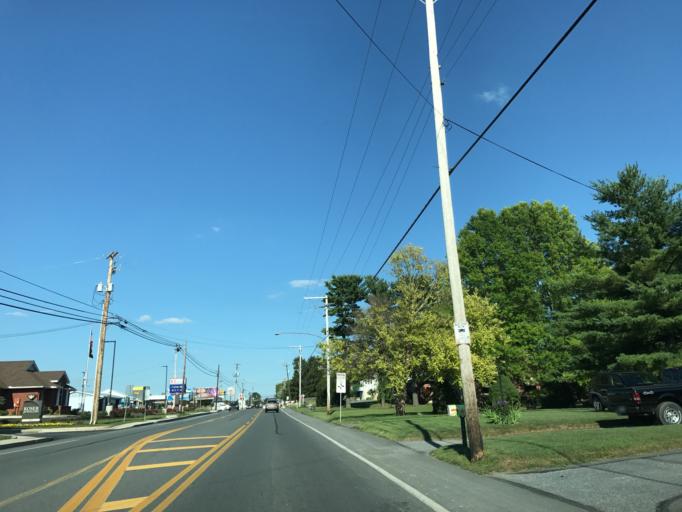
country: US
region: Pennsylvania
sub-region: Lancaster County
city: Mount Joy
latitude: 40.1093
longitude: -76.4845
